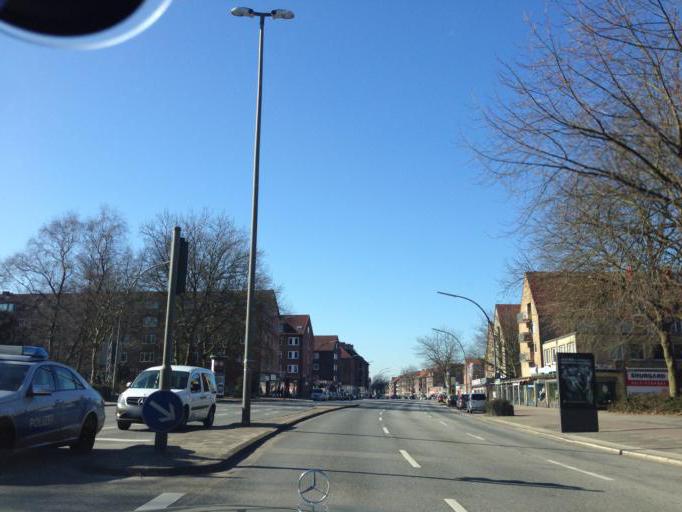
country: DE
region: Hamburg
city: Borgfelde
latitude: 53.5688
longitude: 10.0536
